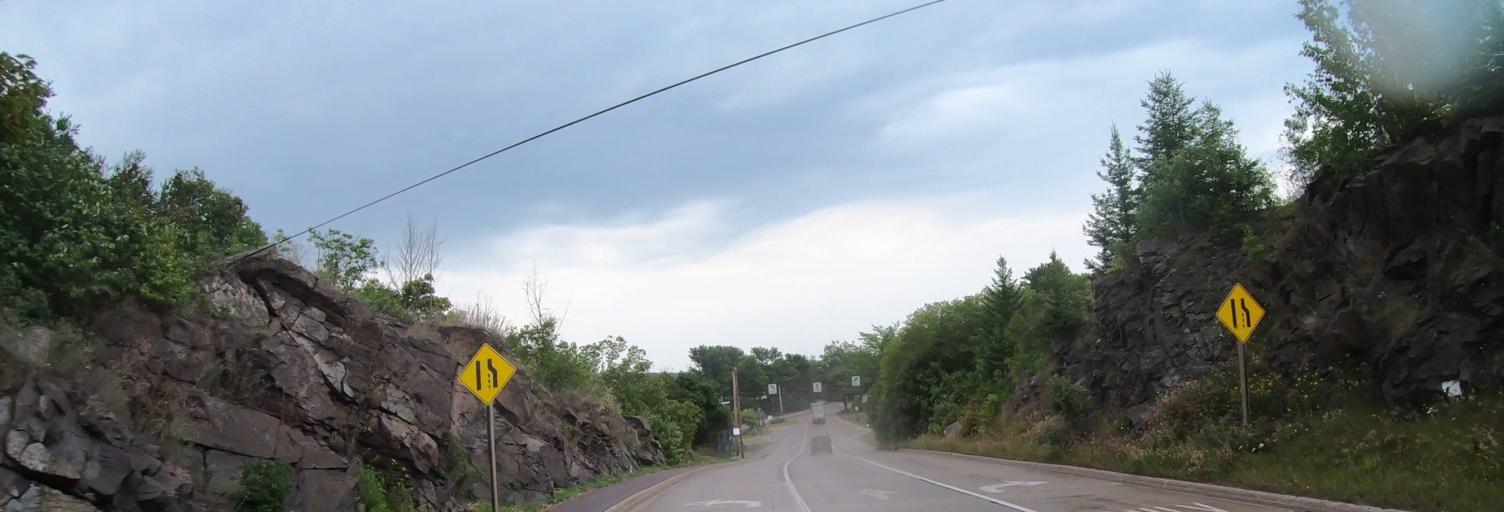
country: US
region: Michigan
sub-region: Houghton County
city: Houghton
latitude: 47.1213
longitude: -88.5645
